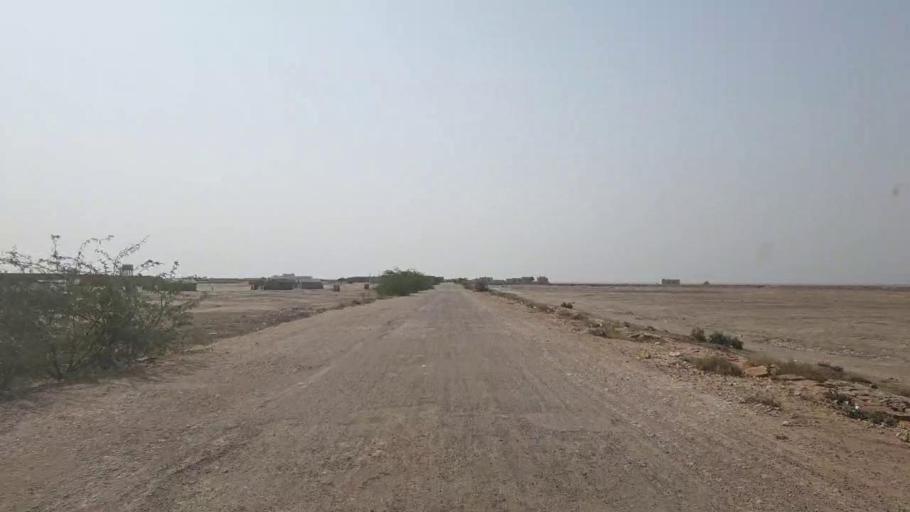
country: PK
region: Sindh
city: Jati
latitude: 24.3402
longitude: 68.5932
